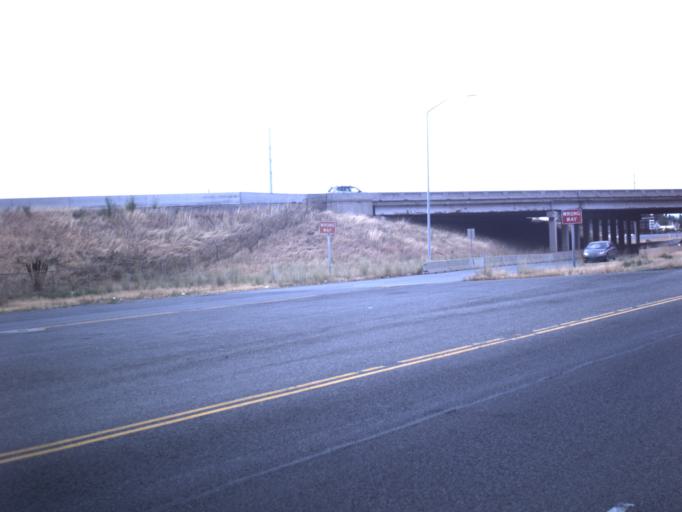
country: US
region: Utah
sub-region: Davis County
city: West Bountiful
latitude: 40.8995
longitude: -111.8920
